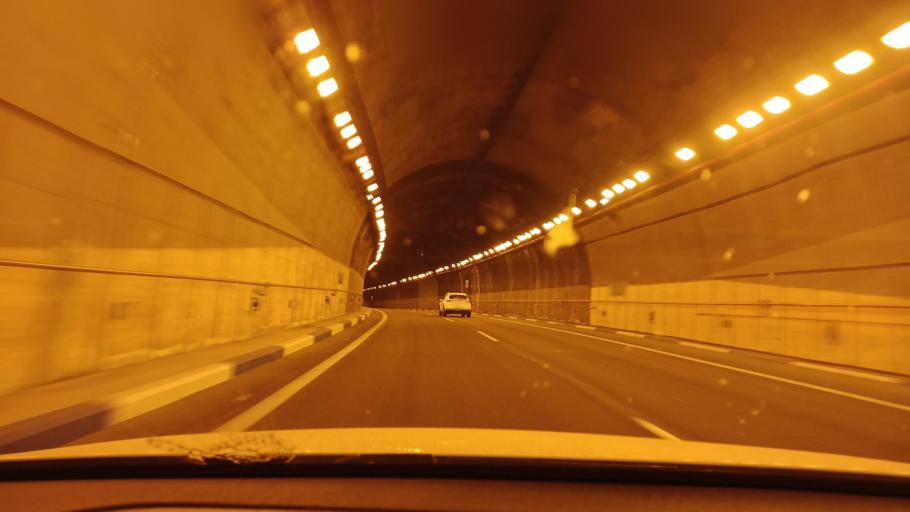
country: ES
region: Valencia
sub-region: Provincia de Valencia
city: L'Olleria
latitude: 38.9226
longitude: -0.5728
